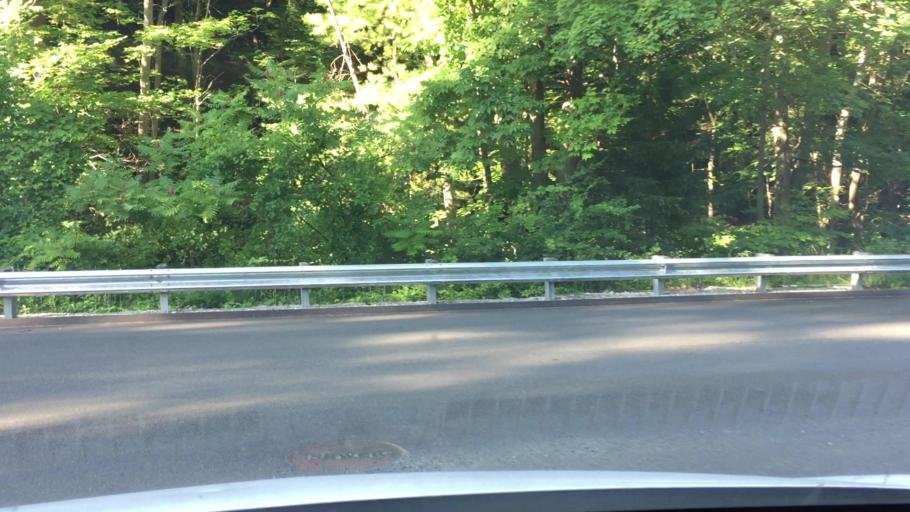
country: US
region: Massachusetts
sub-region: Berkshire County
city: Lee
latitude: 42.2941
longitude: -73.2237
